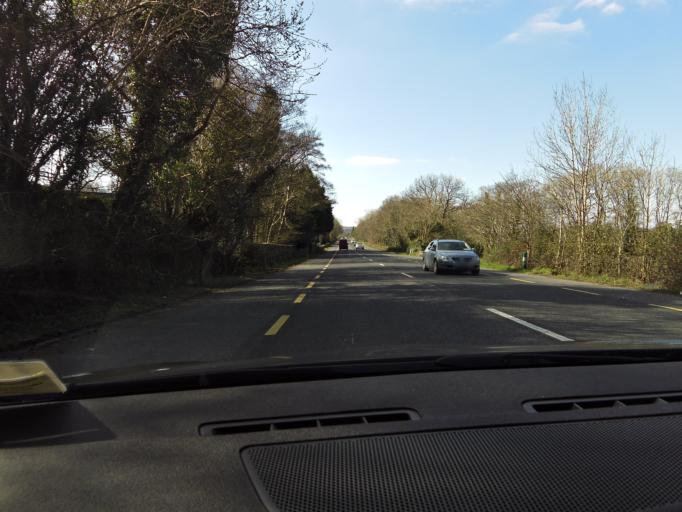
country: IE
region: Connaught
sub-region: County Galway
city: Bearna
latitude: 53.3057
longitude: -9.1151
